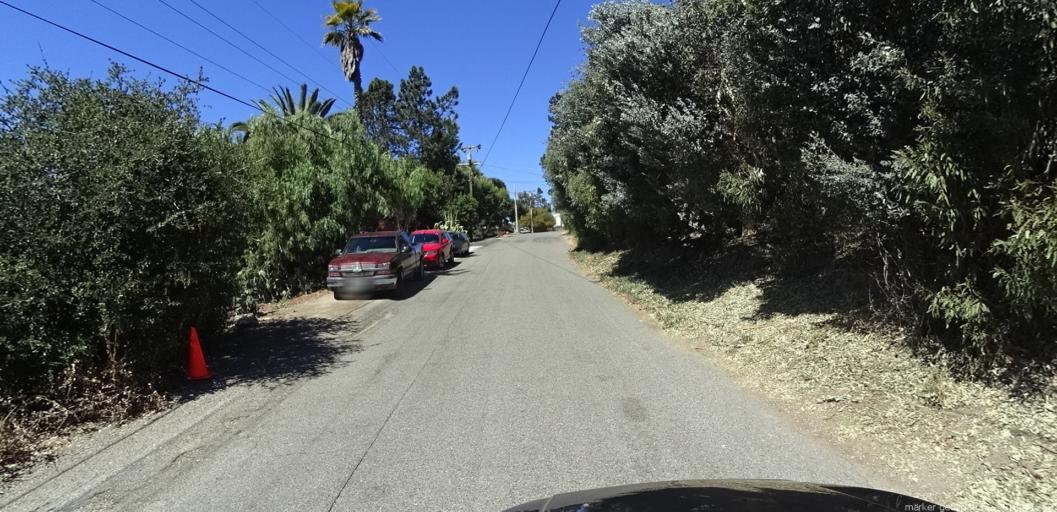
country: US
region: California
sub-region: Monterey County
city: Carmel Valley Village
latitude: 36.4770
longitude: -121.7195
